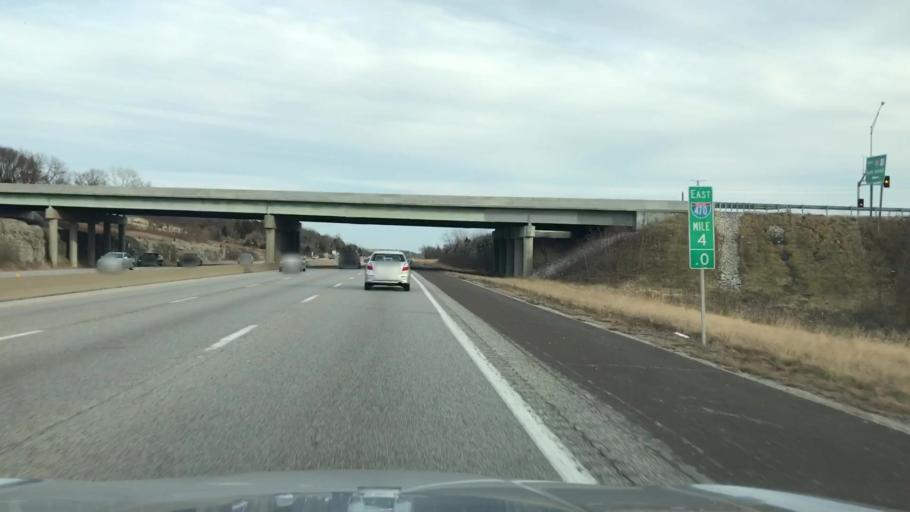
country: US
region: Missouri
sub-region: Jackson County
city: Raytown
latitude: 38.9376
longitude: -94.4726
